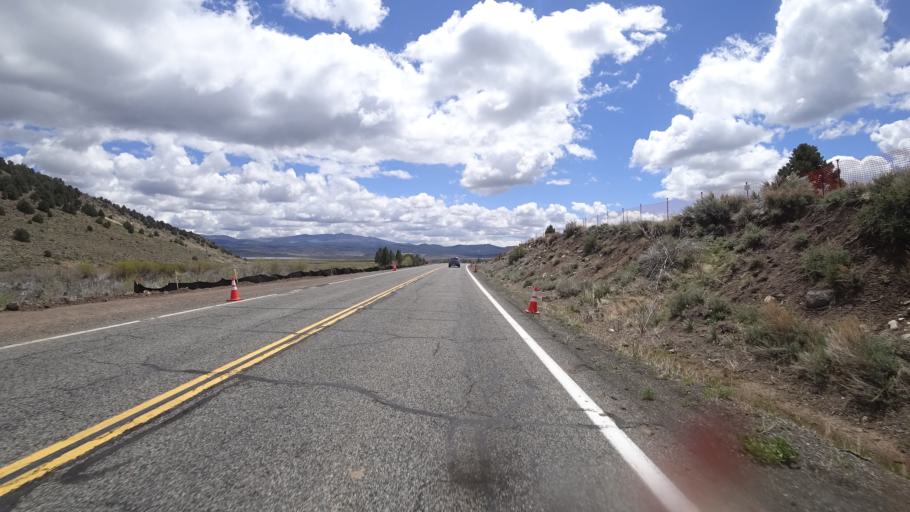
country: US
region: California
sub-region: Mono County
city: Bridgeport
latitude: 38.2796
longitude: -119.2940
